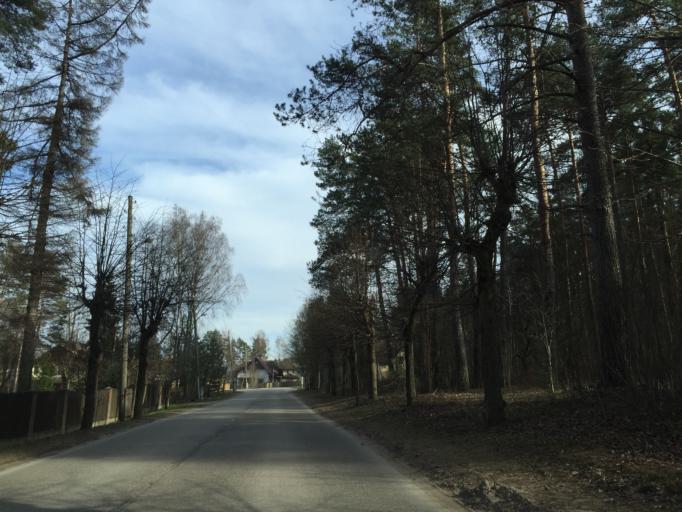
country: LV
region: Ogre
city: Ogre
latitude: 56.8131
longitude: 24.6238
